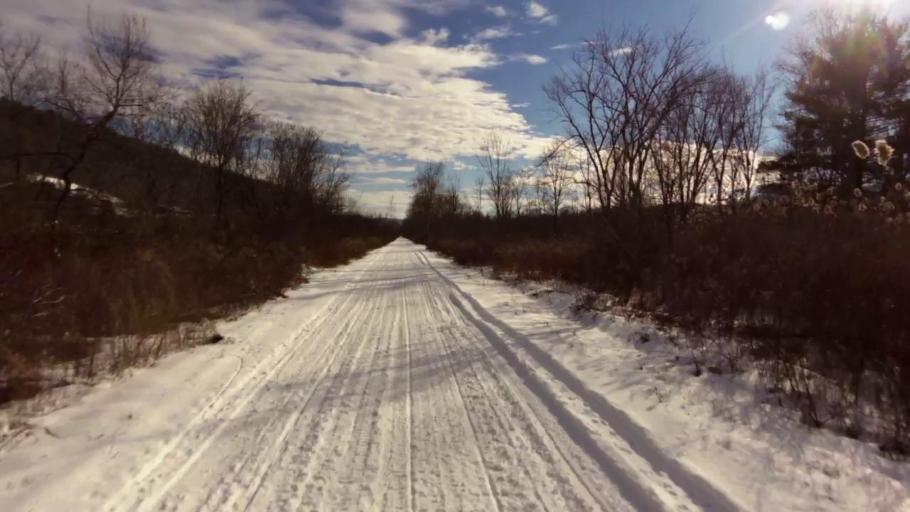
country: US
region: Pennsylvania
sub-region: McKean County
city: Foster Brook
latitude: 42.0188
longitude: -78.6285
